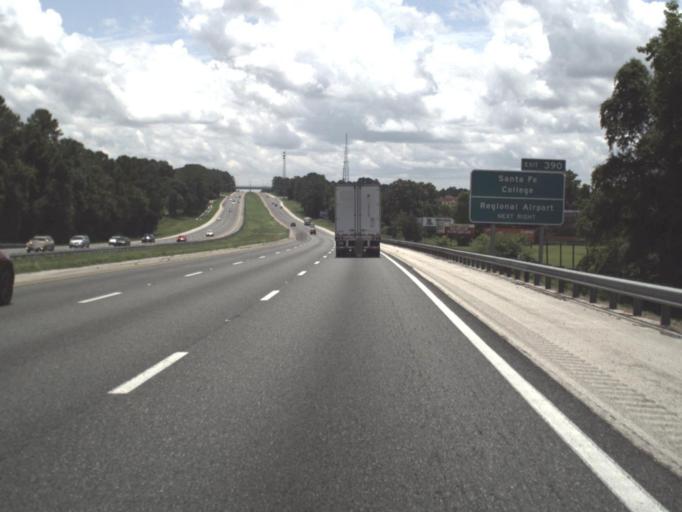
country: US
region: Florida
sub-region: Alachua County
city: Alachua
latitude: 29.6996
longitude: -82.4568
